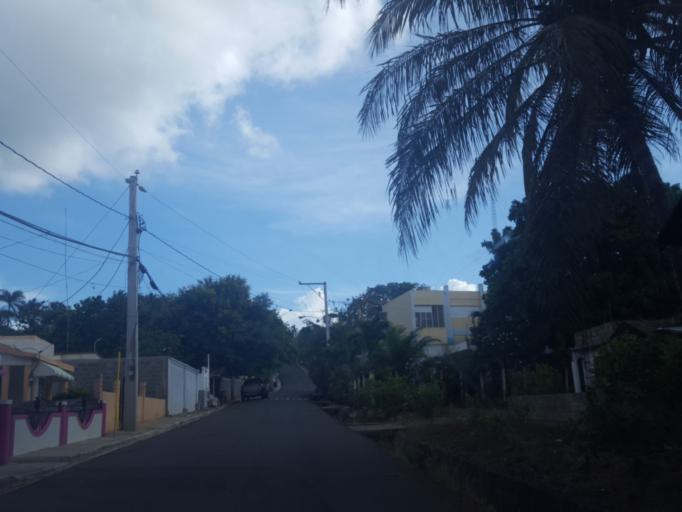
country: DO
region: Santiago
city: Licey al Medio
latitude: 19.3709
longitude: -70.6305
